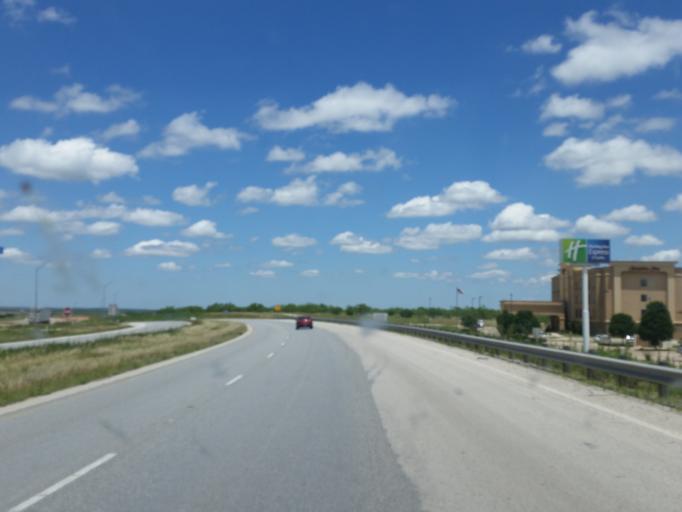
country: US
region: Texas
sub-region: Nolan County
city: Sweetwater
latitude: 32.4511
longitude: -100.3936
